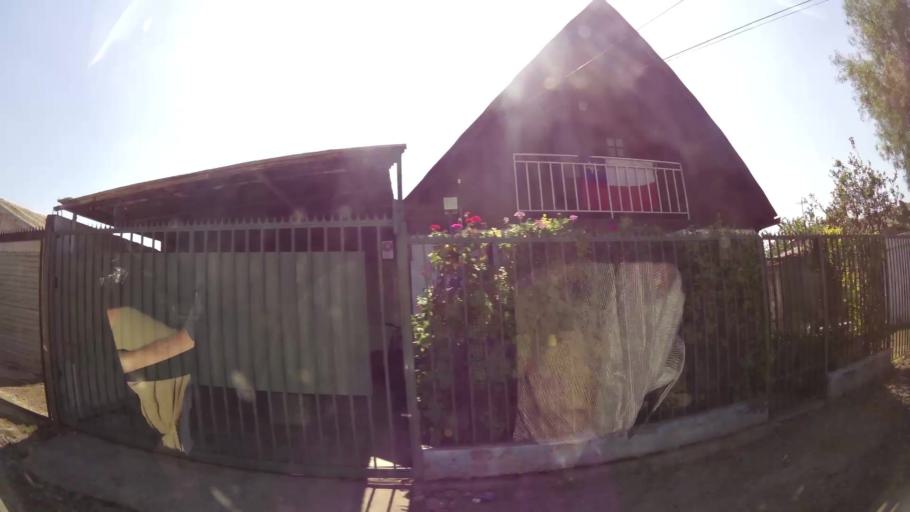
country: CL
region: Santiago Metropolitan
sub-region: Provincia de Talagante
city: Penaflor
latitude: -33.5686
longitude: -70.7979
